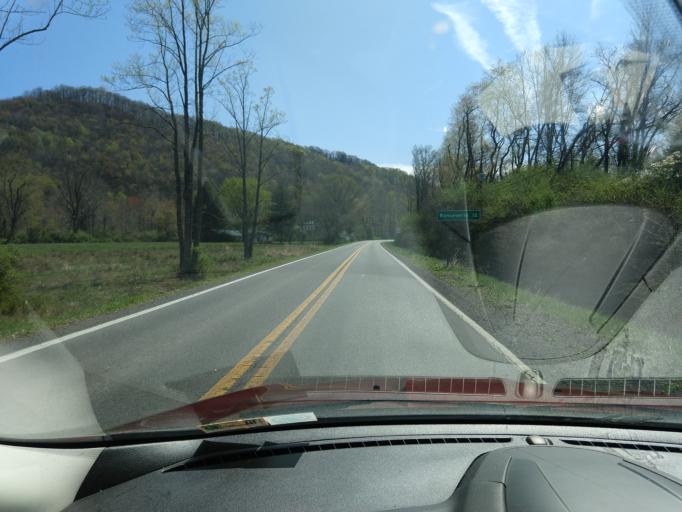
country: US
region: West Virginia
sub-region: Greenbrier County
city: Alderson
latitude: 37.7253
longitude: -80.6330
